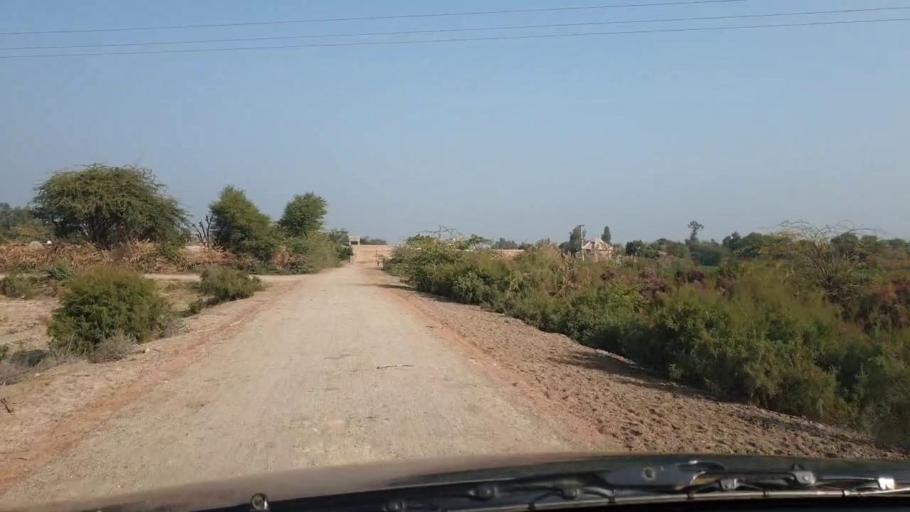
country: PK
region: Sindh
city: Sanghar
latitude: 25.9846
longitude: 68.9519
